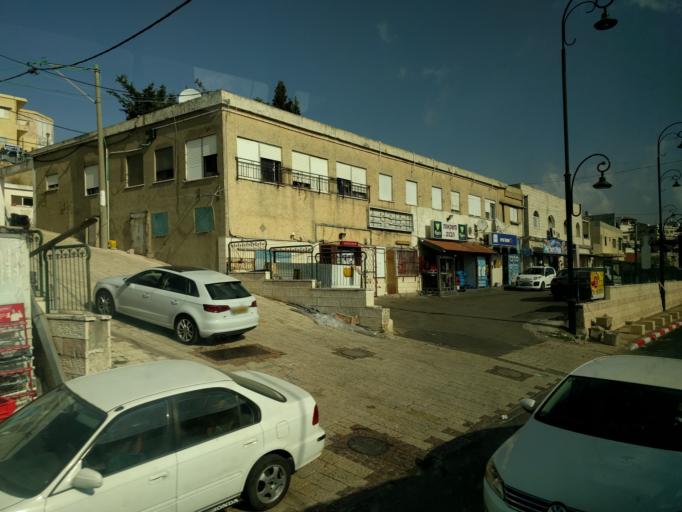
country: IL
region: Haifa
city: Daliyat el Karmil
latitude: 32.7170
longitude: 35.0659
